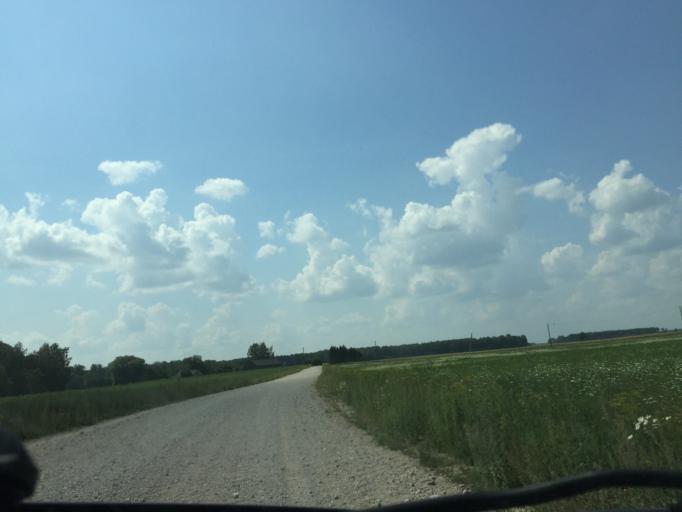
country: LT
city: Zagare
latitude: 56.3972
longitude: 23.2234
